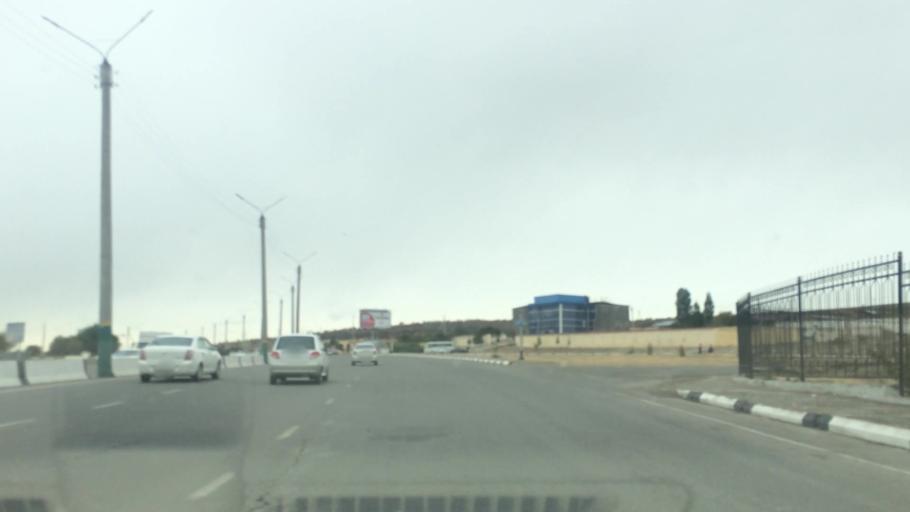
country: UZ
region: Samarqand
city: Jomboy
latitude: 39.6756
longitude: 67.0431
